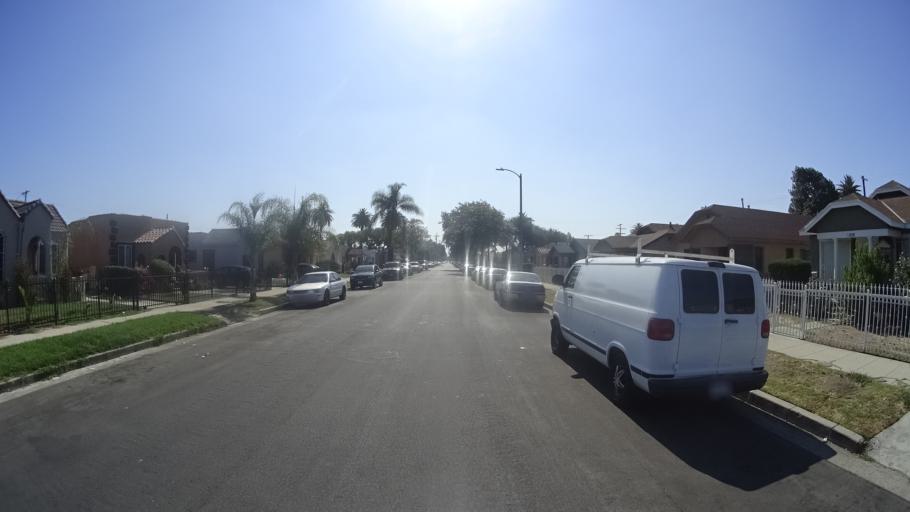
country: US
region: California
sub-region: Los Angeles County
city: Westmont
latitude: 33.9814
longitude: -118.3037
